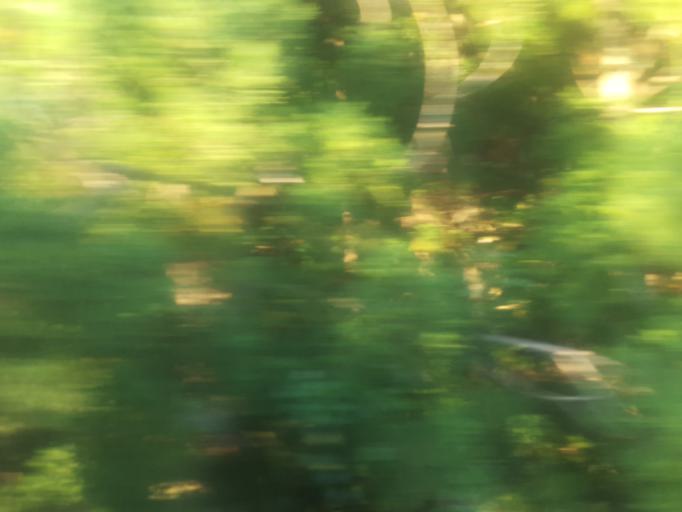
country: JP
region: Toyama
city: Kamiichi
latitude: 36.5751
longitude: 137.3690
